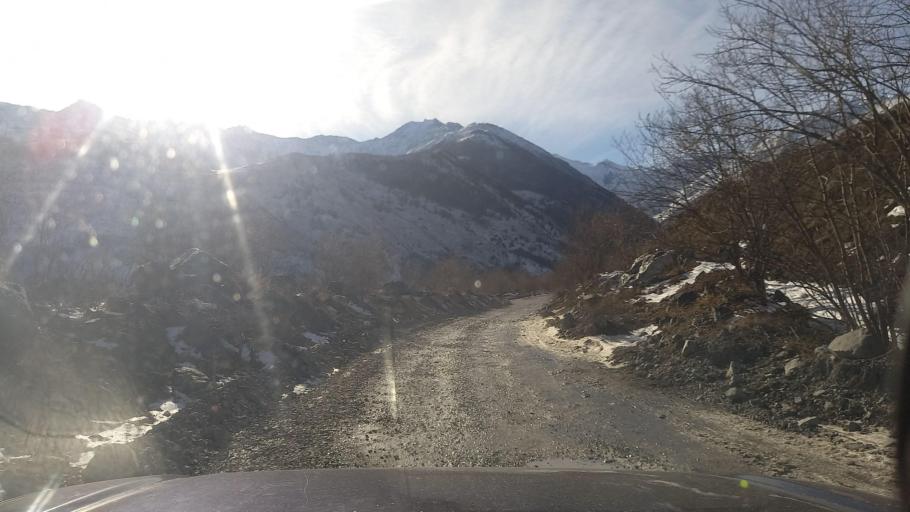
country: RU
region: Ingushetiya
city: Dzhayrakh
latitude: 42.8449
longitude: 44.5156
